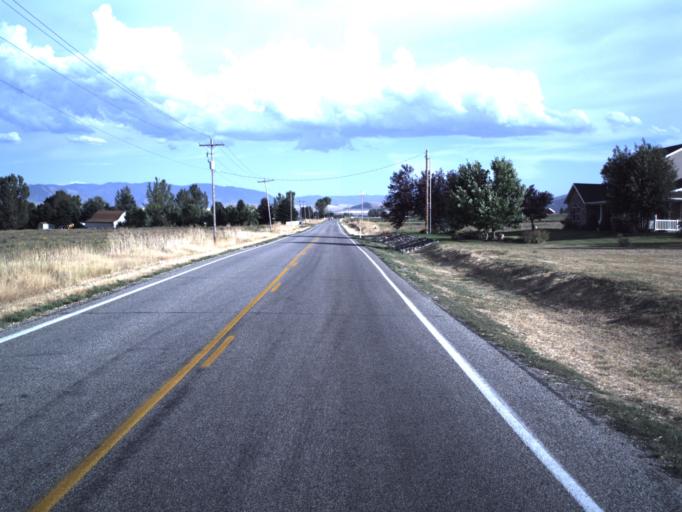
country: US
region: Utah
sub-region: Cache County
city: Wellsville
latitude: 41.6707
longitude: -111.9537
